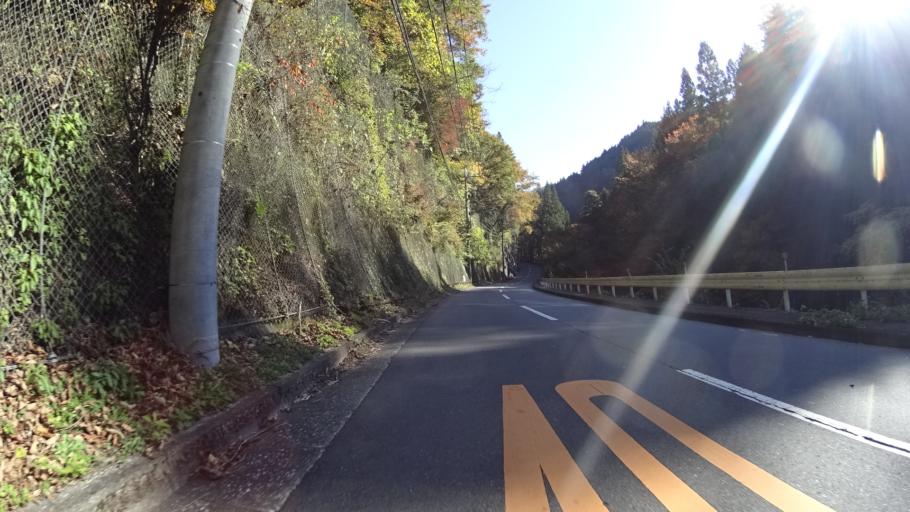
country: JP
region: Yamanashi
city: Uenohara
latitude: 35.7090
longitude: 139.0954
